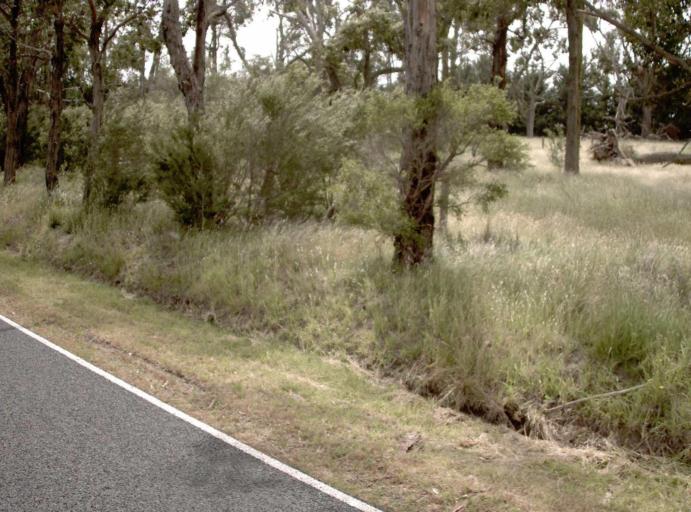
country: AU
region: Victoria
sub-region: Latrobe
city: Moe
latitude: -38.1327
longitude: 146.1486
